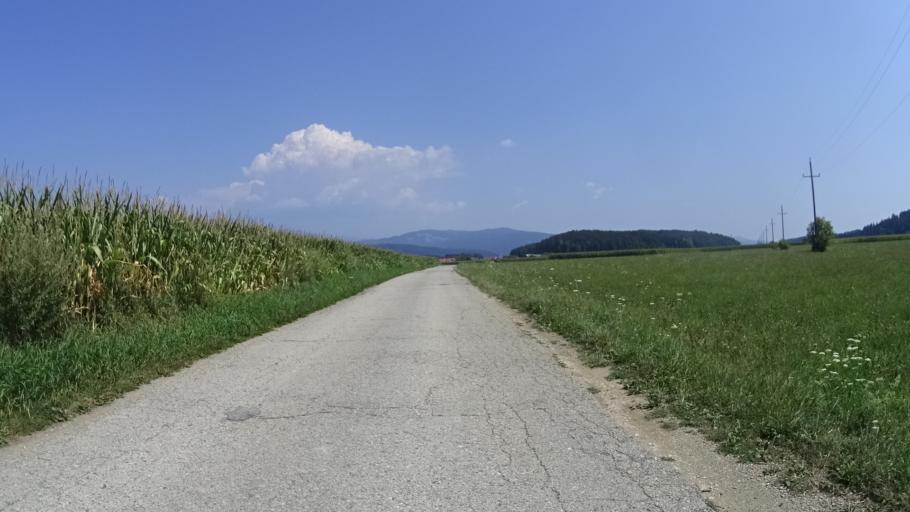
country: AT
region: Carinthia
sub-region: Politischer Bezirk Volkermarkt
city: Globasnitz
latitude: 46.5572
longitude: 14.7310
